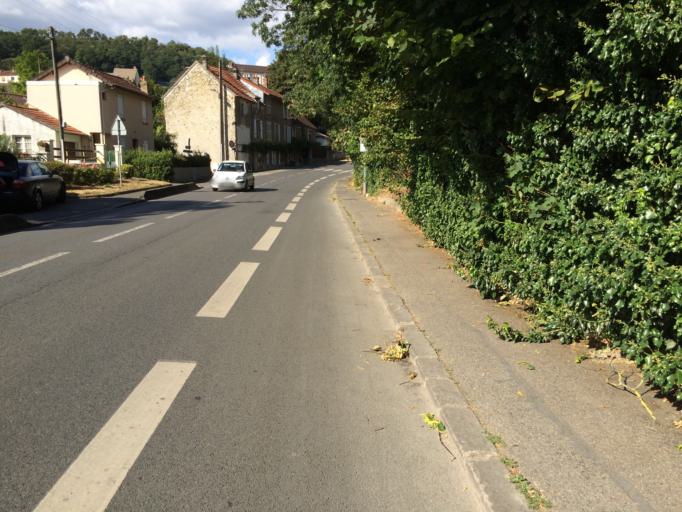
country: FR
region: Ile-de-France
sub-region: Departement de l'Essonne
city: Villebon-sur-Yvette
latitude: 48.7021
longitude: 2.2213
